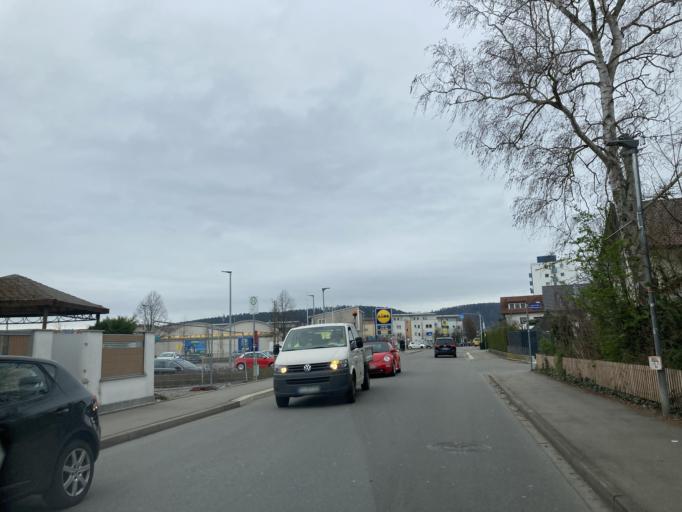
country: DE
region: Baden-Wuerttemberg
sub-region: Tuebingen Region
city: Rottenburg
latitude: 48.4807
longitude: 8.9444
